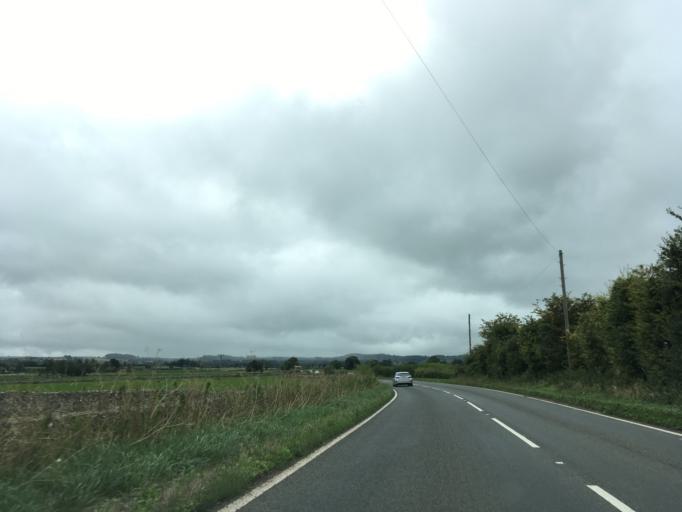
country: GB
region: England
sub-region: Bath and North East Somerset
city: Cameley
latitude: 51.2891
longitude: -2.5526
